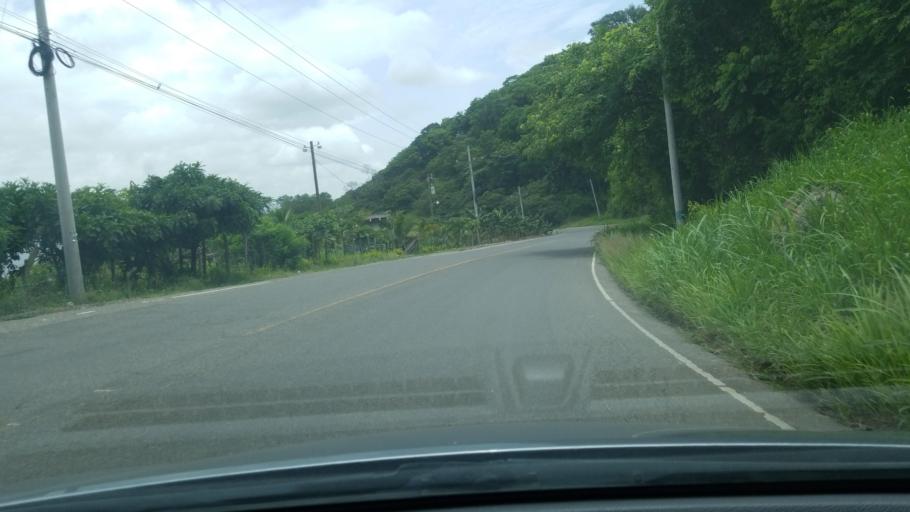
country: HN
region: Copan
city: Ojos de Agua
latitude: 14.6742
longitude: -88.8261
